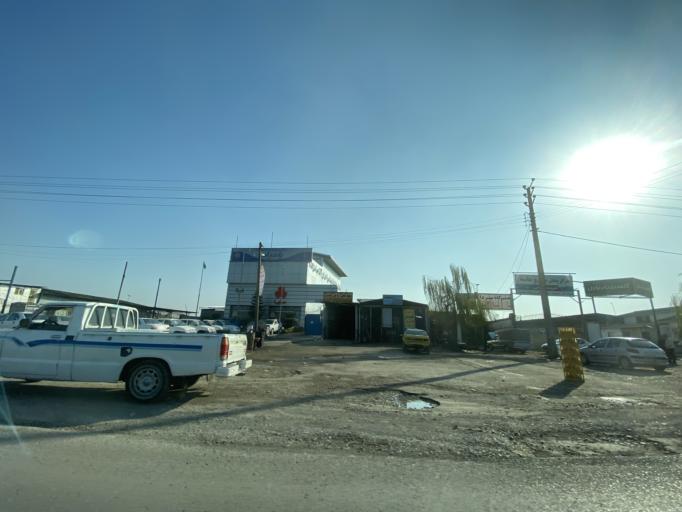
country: IR
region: Mazandaran
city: Babol
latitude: 36.5289
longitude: 52.6294
